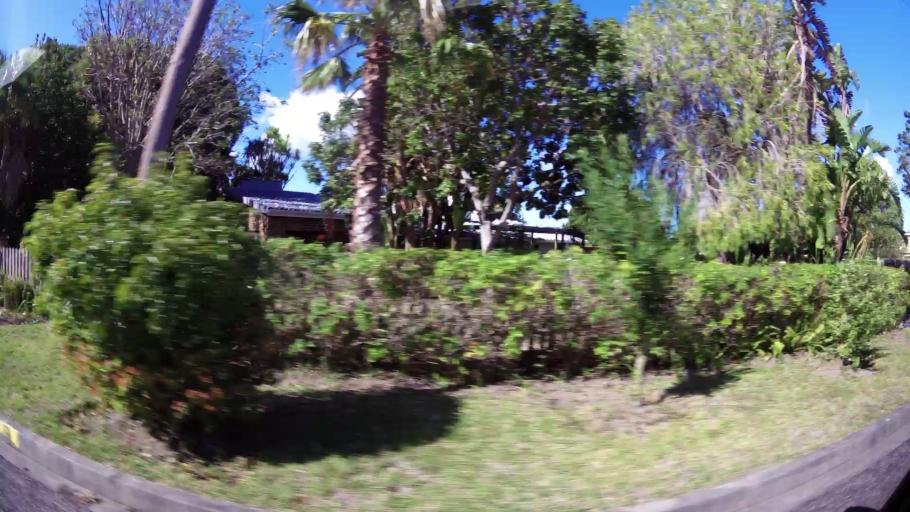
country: ZA
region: Western Cape
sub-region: Eden District Municipality
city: George
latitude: -33.9515
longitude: 22.4747
